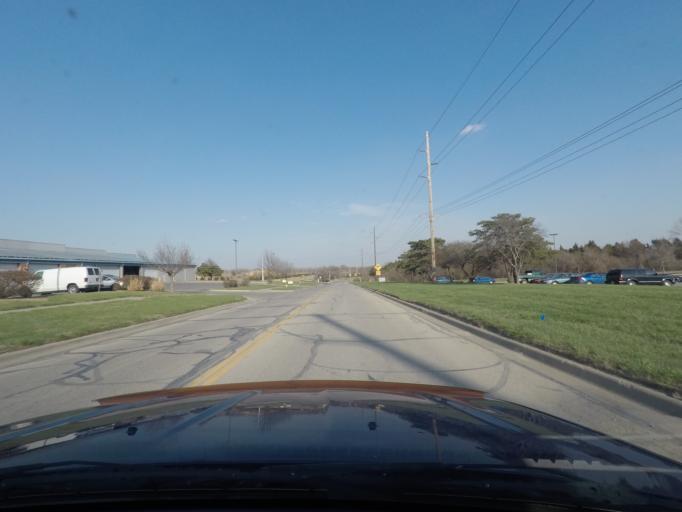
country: US
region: Kansas
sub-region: Douglas County
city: Lawrence
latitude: 39.0006
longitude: -95.2638
